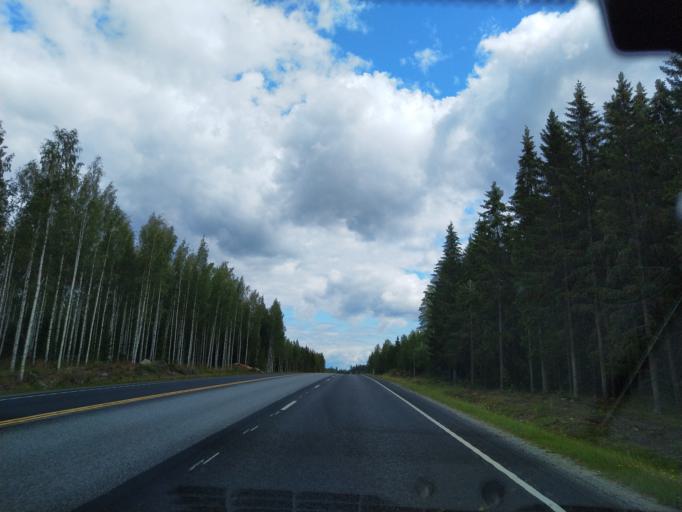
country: FI
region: Pirkanmaa
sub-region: Tampere
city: Nokia
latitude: 61.4010
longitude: 23.2633
